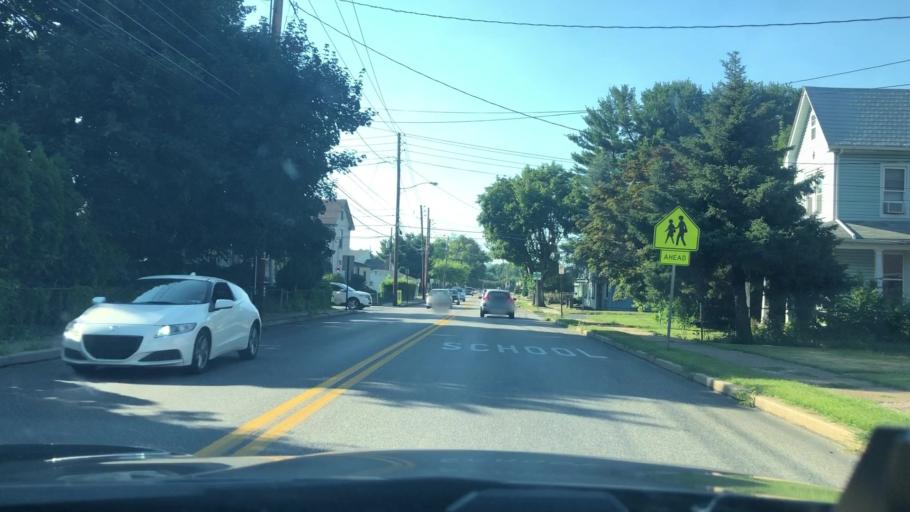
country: US
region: Pennsylvania
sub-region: Cumberland County
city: Mechanicsburg
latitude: 40.2178
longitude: -77.0047
